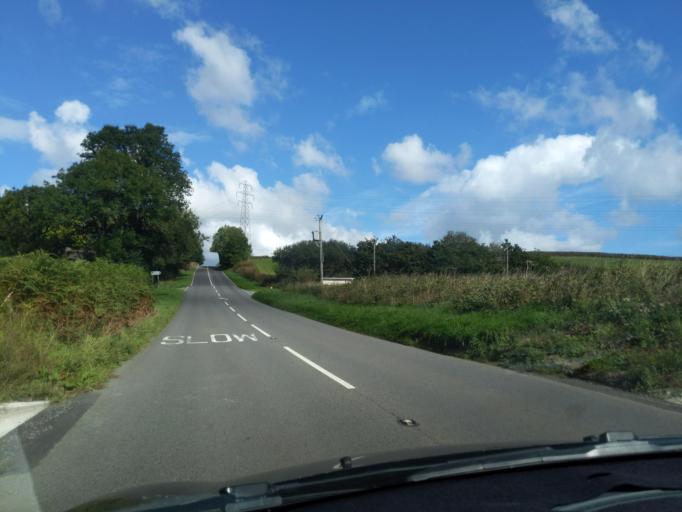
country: GB
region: England
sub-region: Devon
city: Holsworthy
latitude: 50.8913
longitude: -4.2748
